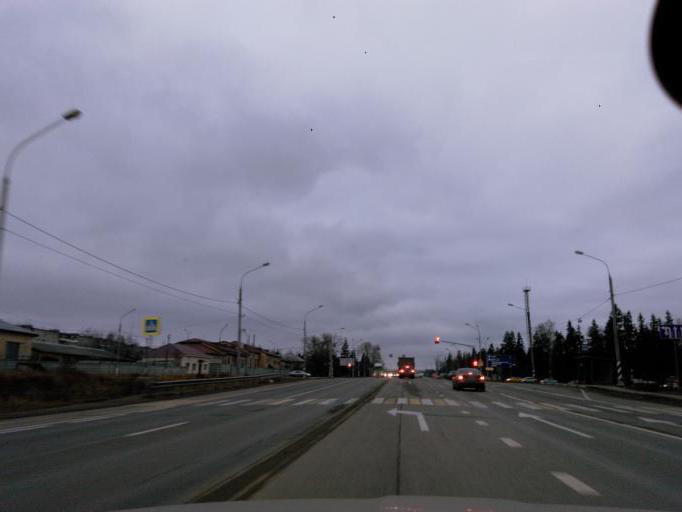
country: RU
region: Moskovskaya
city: Radumlya
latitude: 56.0719
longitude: 37.1319
